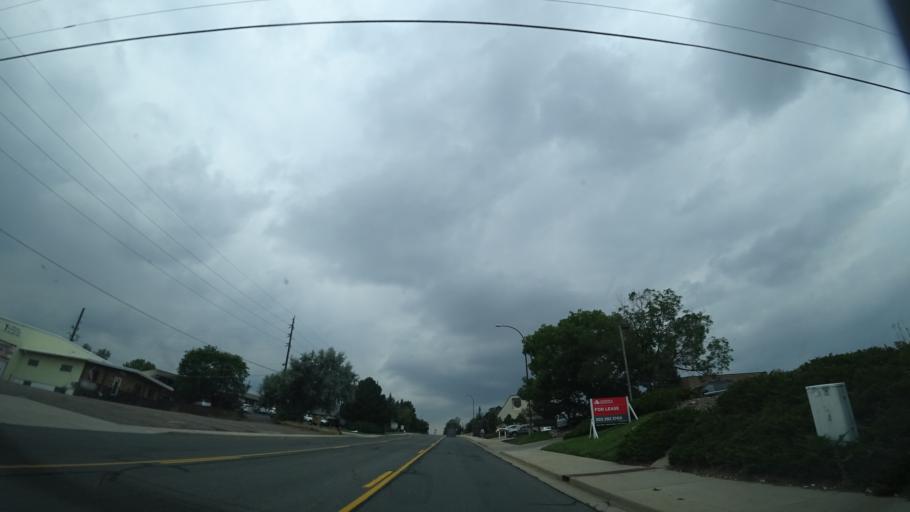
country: US
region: Colorado
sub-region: Jefferson County
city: West Pleasant View
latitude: 39.7122
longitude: -105.1395
